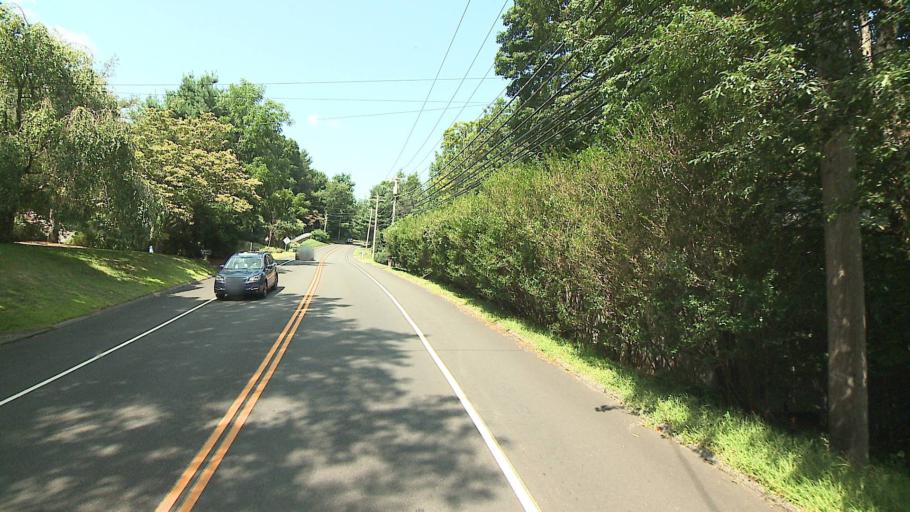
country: US
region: Connecticut
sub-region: Fairfield County
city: Trumbull
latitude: 41.2284
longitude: -73.2592
